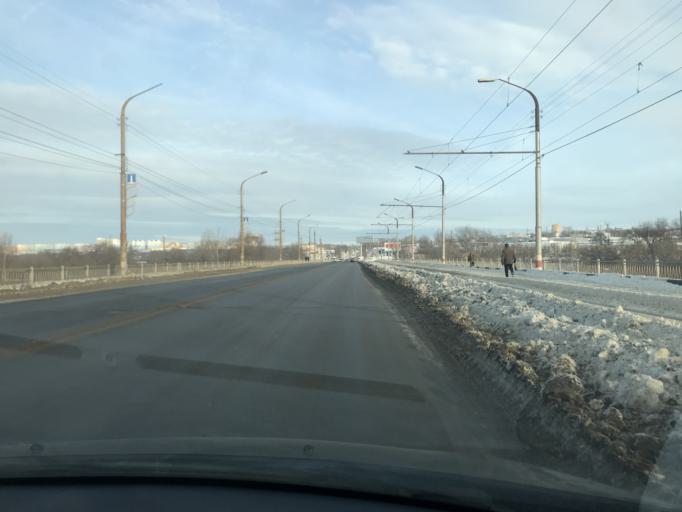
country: RU
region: Ulyanovsk
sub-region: Ulyanovskiy Rayon
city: Ulyanovsk
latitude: 54.3241
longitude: 48.3571
